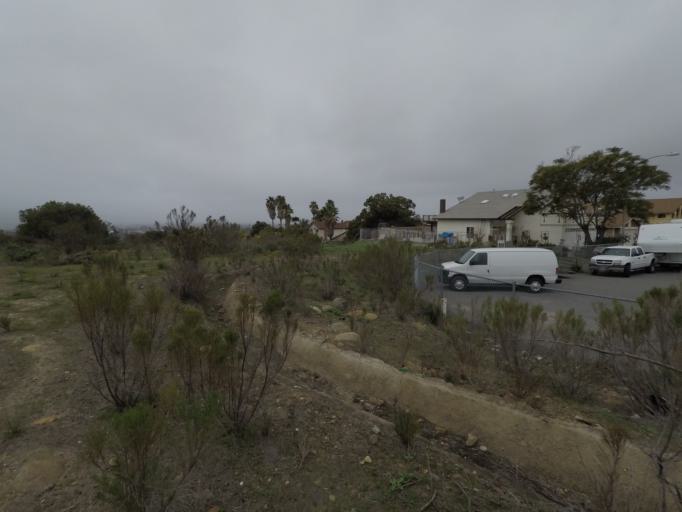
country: MX
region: Baja California
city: Tijuana
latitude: 32.5567
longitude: -117.0380
